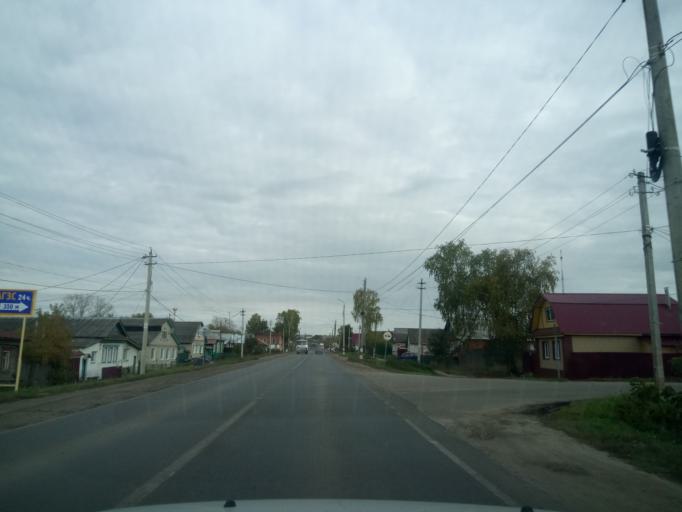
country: RU
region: Nizjnij Novgorod
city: Lukoyanov
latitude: 55.0310
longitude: 44.4844
